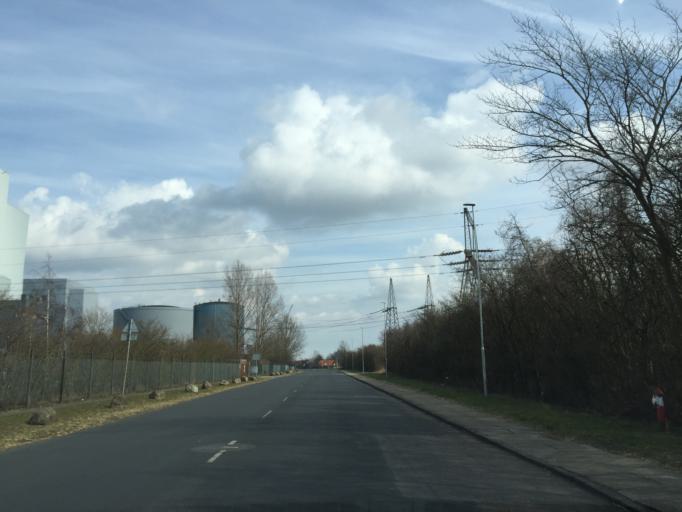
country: DK
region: South Denmark
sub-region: Odense Kommune
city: Stige
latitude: 55.4272
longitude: 10.4072
